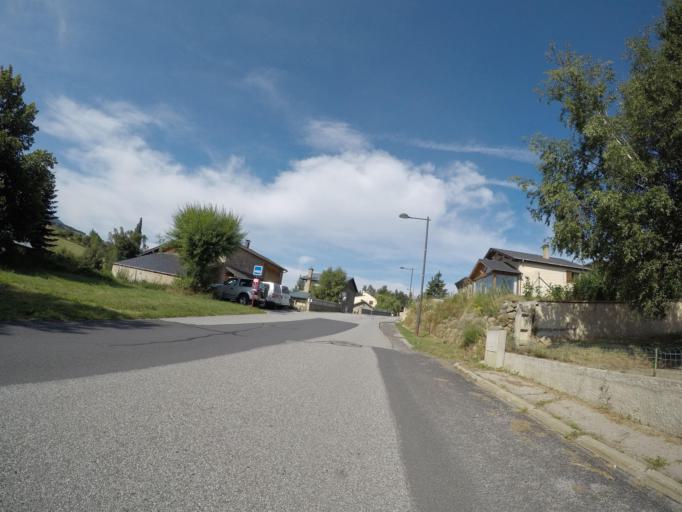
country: ES
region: Catalonia
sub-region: Provincia de Girona
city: Llivia
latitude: 42.5009
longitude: 2.1075
